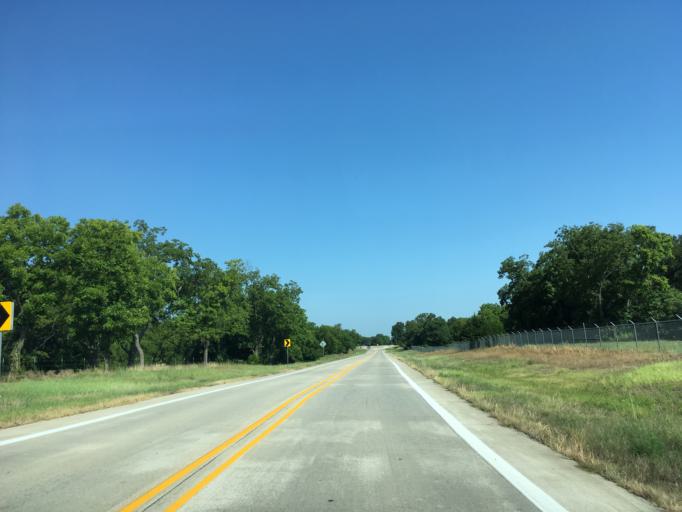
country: US
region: Texas
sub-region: Collin County
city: Fairview
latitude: 33.1607
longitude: -96.5914
